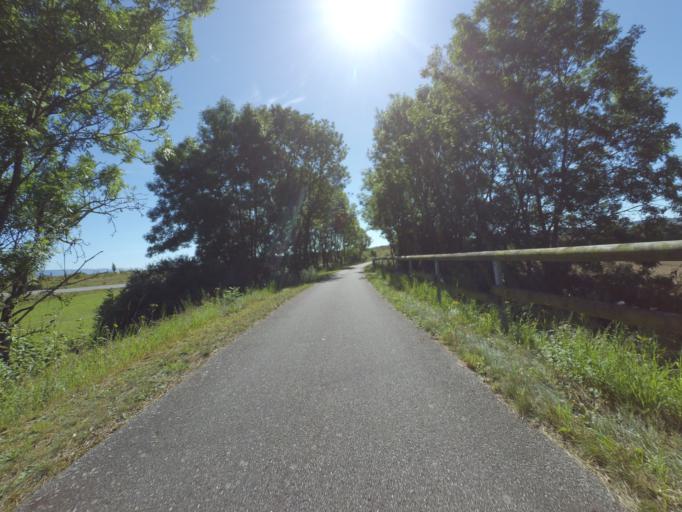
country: DE
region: Rheinland-Pfalz
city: Hasborn
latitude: 50.0642
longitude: 6.9036
